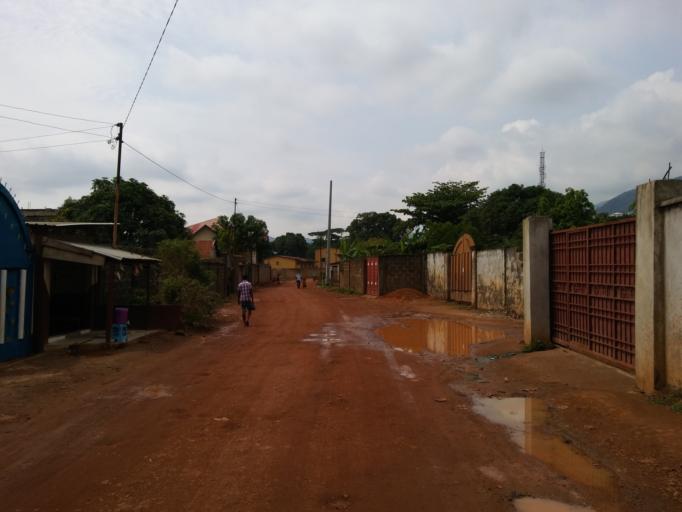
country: SL
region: Western Area
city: Hastings
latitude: 8.3882
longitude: -13.1463
